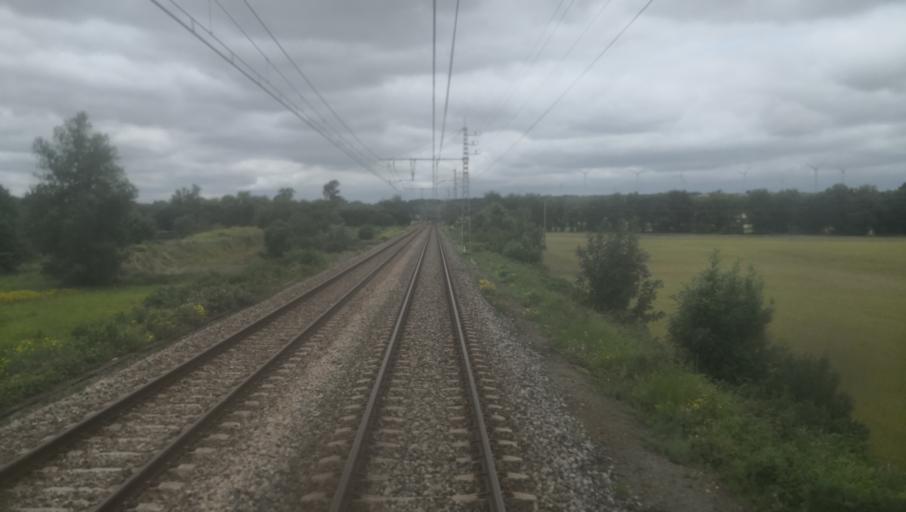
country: FR
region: Midi-Pyrenees
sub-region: Departement de la Haute-Garonne
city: Avignonet-Lauragais
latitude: 43.3548
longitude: 1.8092
